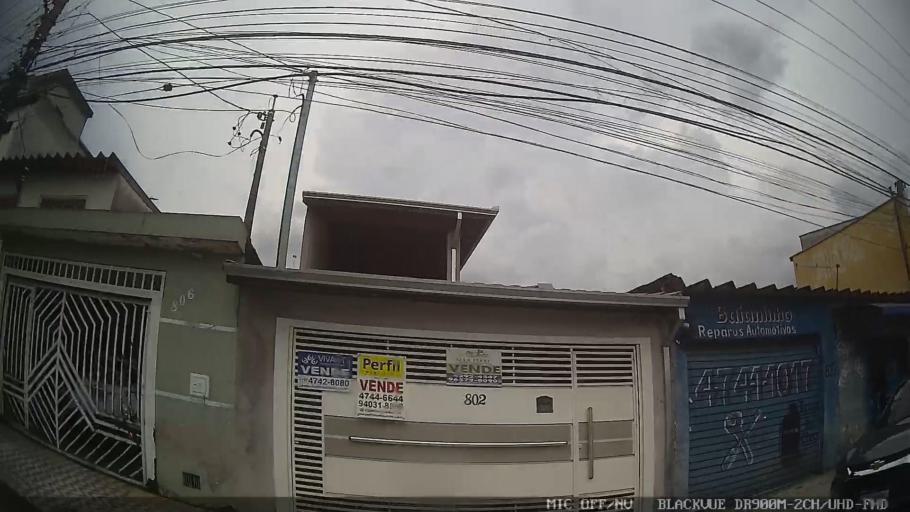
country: BR
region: Sao Paulo
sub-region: Suzano
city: Suzano
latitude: -23.5410
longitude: -46.2987
